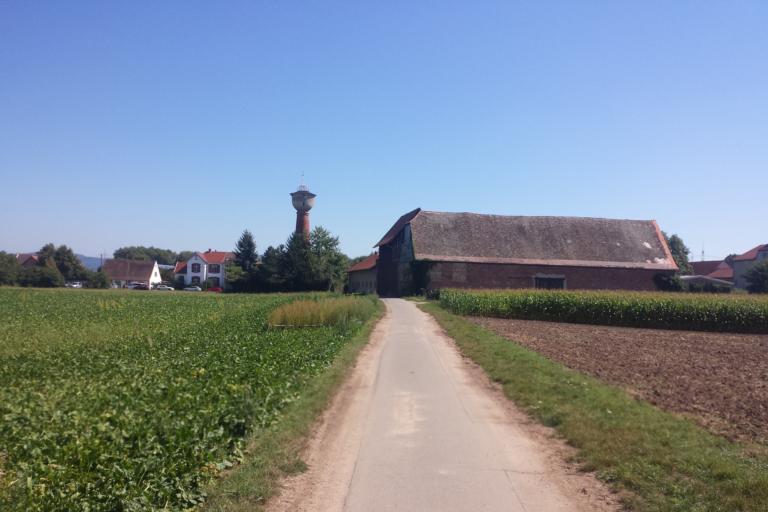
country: DE
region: Hesse
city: Viernheim
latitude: 49.5129
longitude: 8.5738
